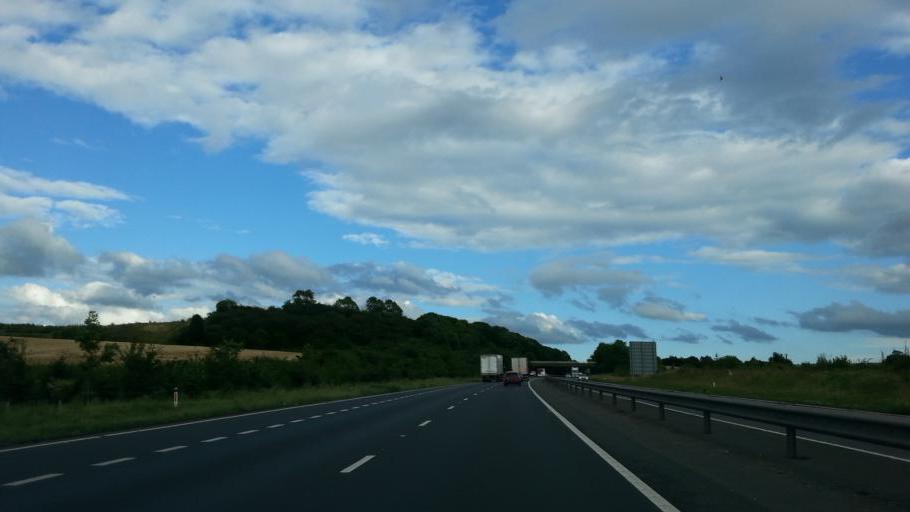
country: GB
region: England
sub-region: Nottinghamshire
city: Tuxford
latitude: 53.2540
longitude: -0.9189
